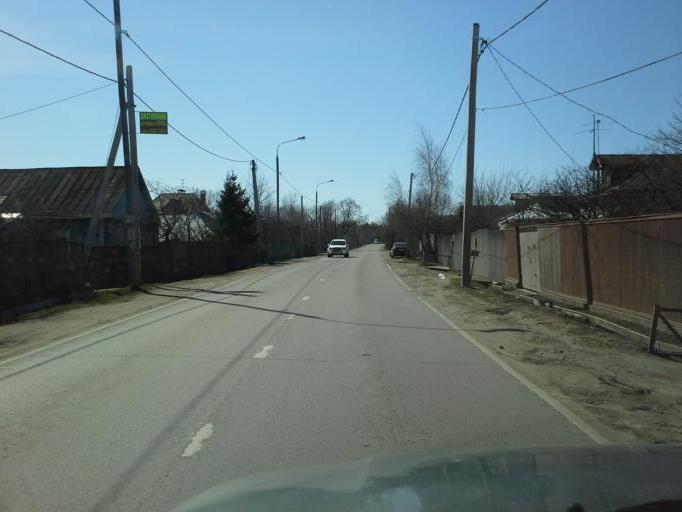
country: RU
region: Moskovskaya
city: Kokoshkino
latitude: 55.6025
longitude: 37.1876
